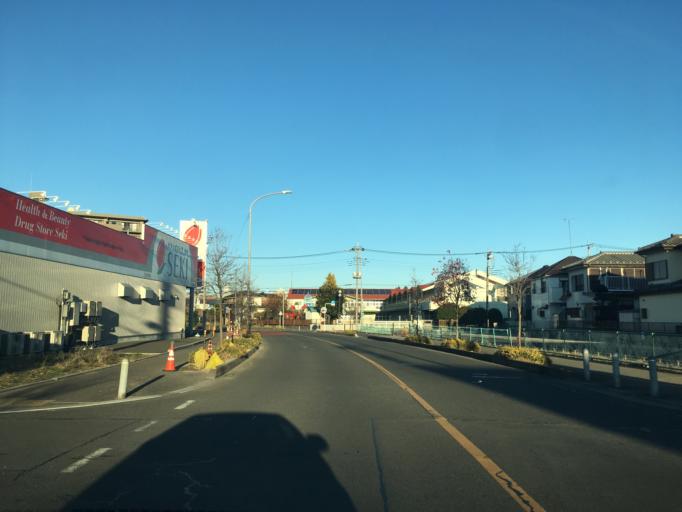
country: JP
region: Saitama
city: Sayama
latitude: 35.8190
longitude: 139.4071
